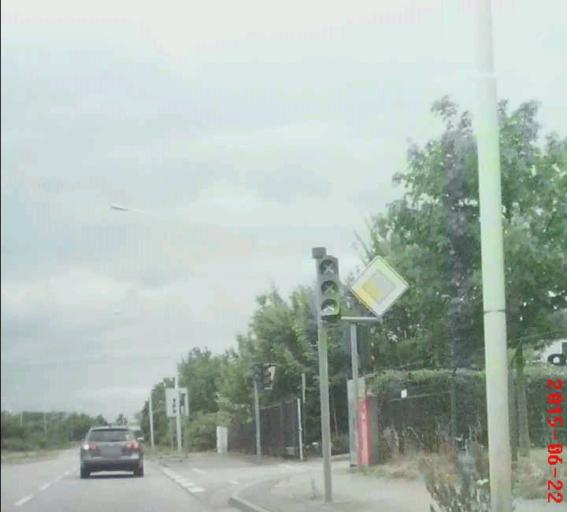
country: DE
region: Saxony-Anhalt
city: Angersdorf
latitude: 51.4672
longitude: 11.8944
